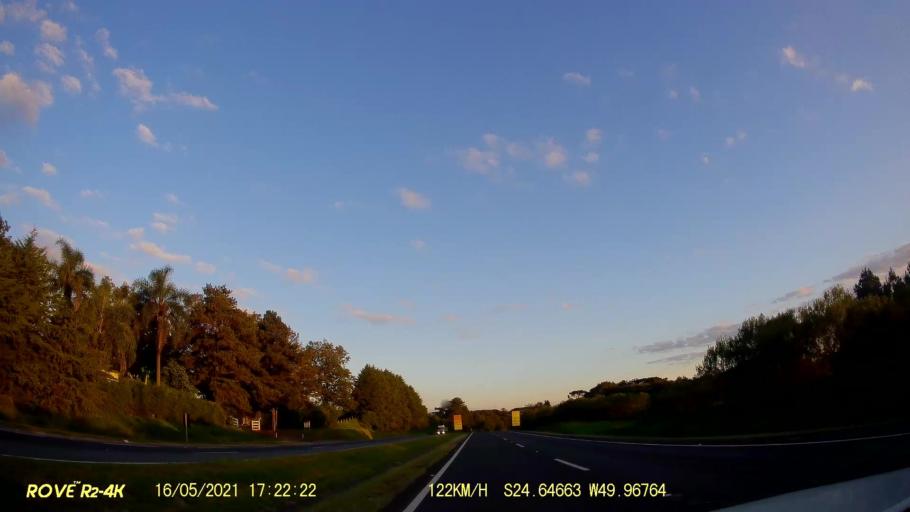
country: BR
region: Parana
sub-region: Pirai Do Sul
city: Pirai do Sul
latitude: -24.6469
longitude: -49.9676
